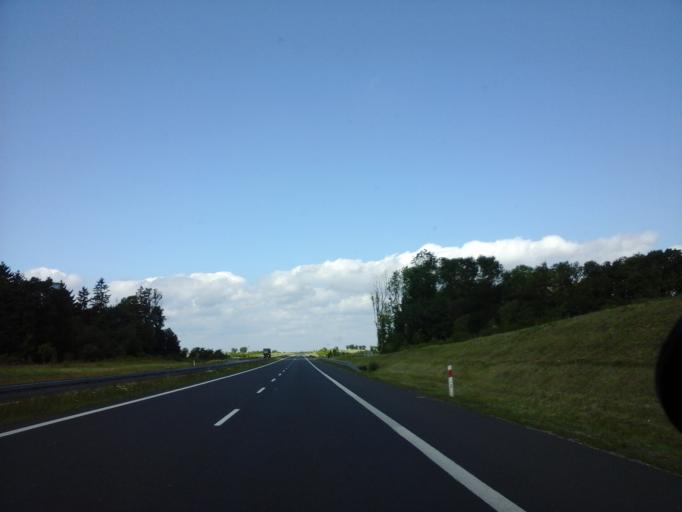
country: PL
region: West Pomeranian Voivodeship
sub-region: Powiat stargardzki
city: Stargard Szczecinski
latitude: 53.3111
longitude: 15.0003
